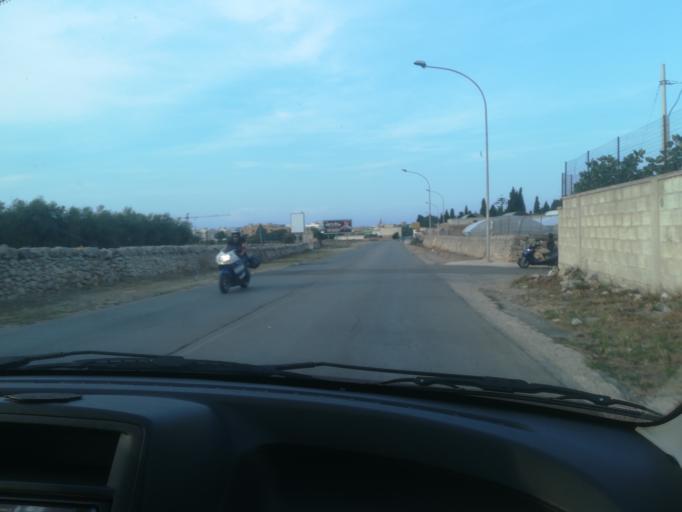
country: IT
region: Apulia
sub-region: Provincia di Bari
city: Monopoli
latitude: 40.9407
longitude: 17.2962
